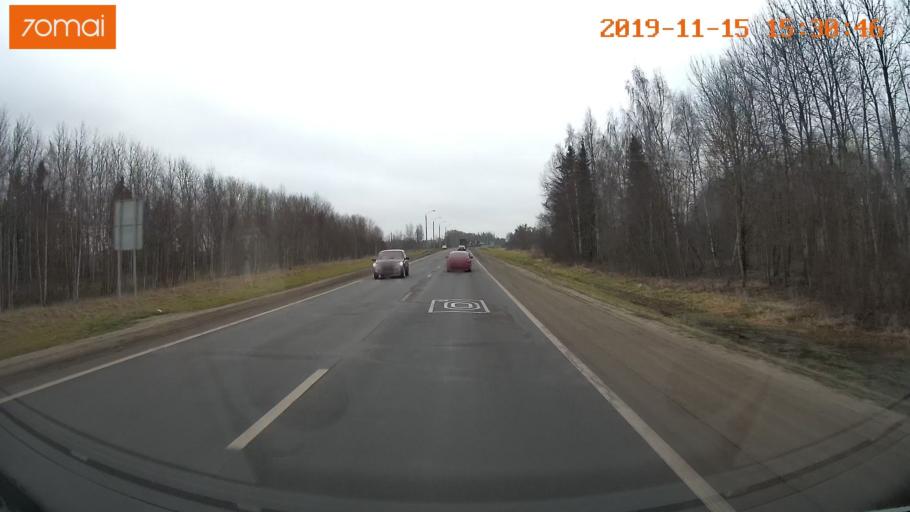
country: RU
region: Jaroslavl
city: Danilov
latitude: 58.1068
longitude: 40.1115
